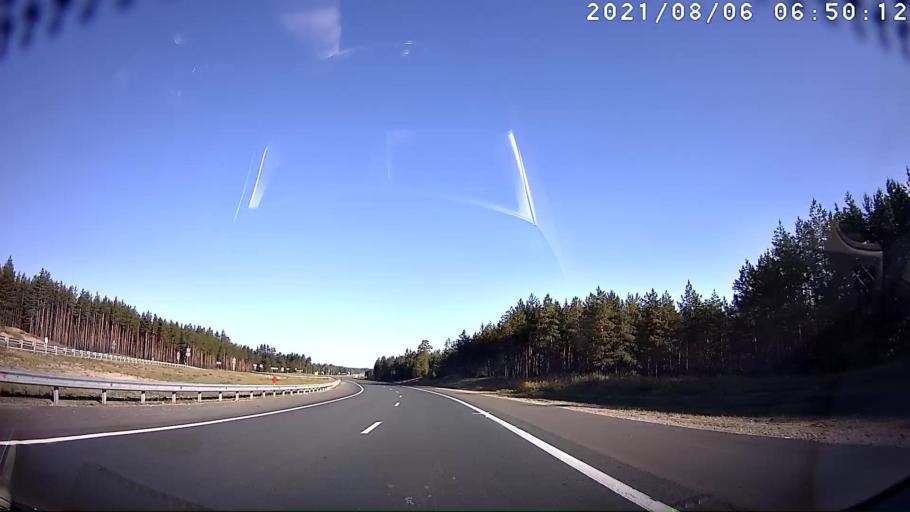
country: RU
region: Mariy-El
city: Surok
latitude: 56.4021
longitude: 48.1656
